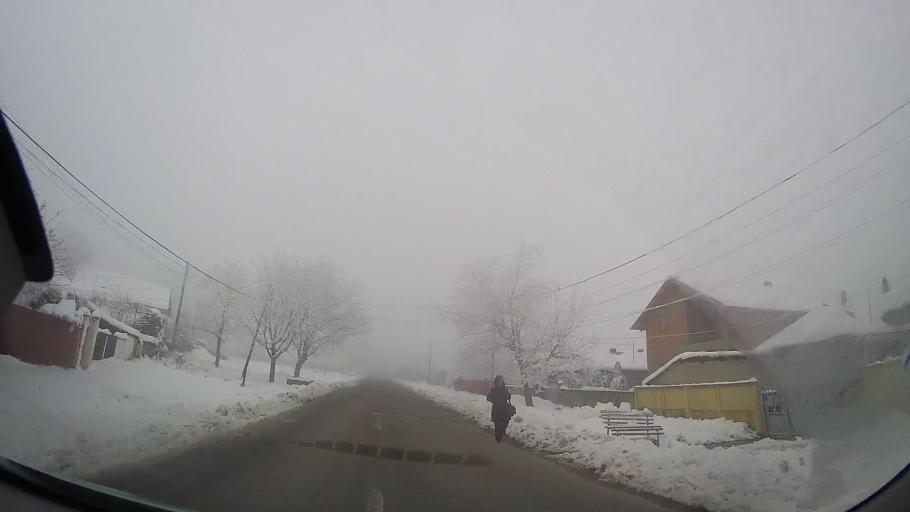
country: RO
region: Neamt
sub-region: Comuna Sabaoani
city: Sabaoani
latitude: 47.0205
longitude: 26.8646
